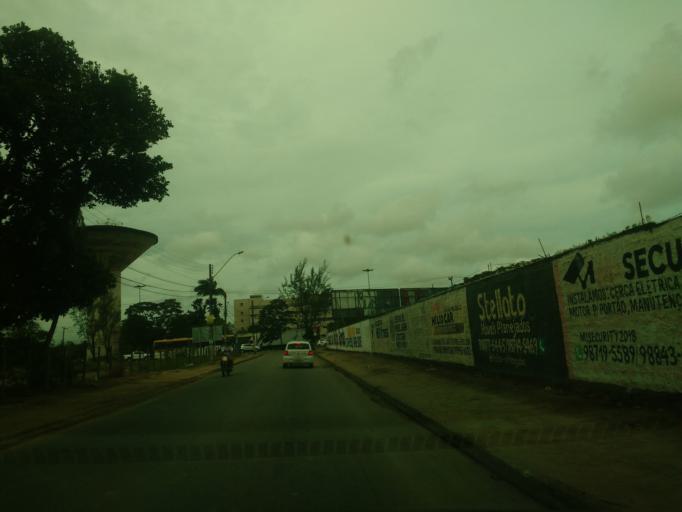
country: BR
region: Alagoas
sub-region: Satuba
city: Satuba
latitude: -9.5603
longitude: -35.7813
